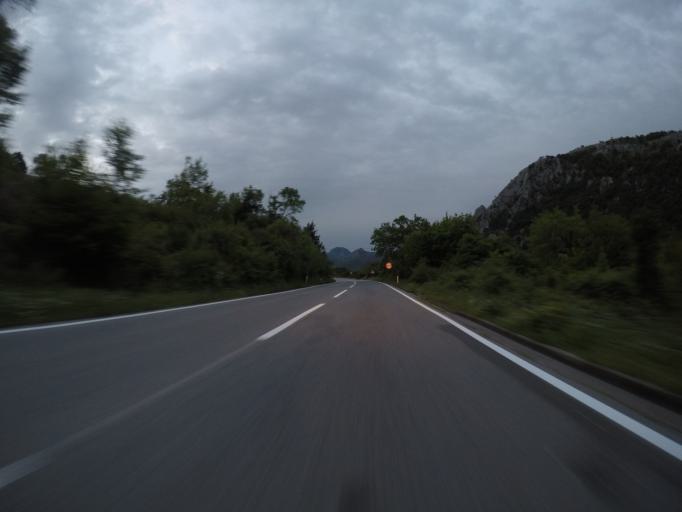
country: ME
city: Petrovac na Moru
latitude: 42.2028
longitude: 18.9594
